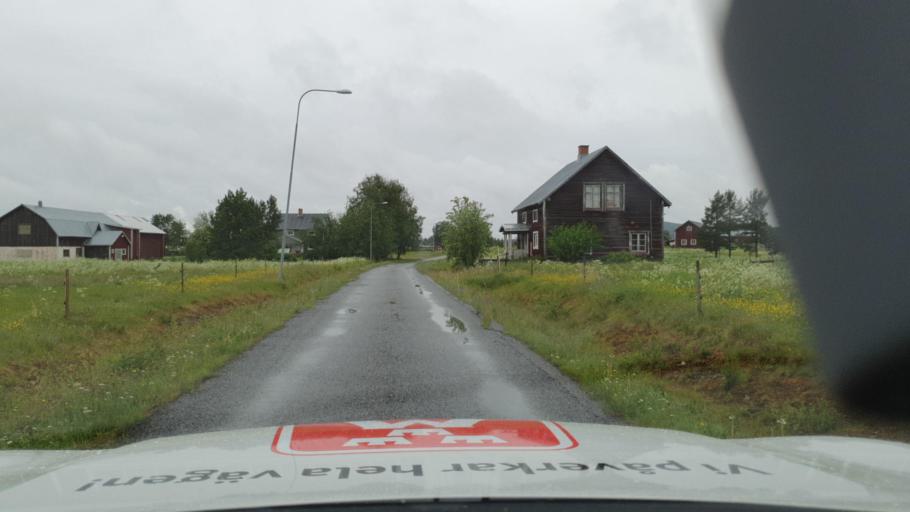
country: SE
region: Vaesterbotten
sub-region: Asele Kommun
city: Asele
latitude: 63.9398
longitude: 17.2739
